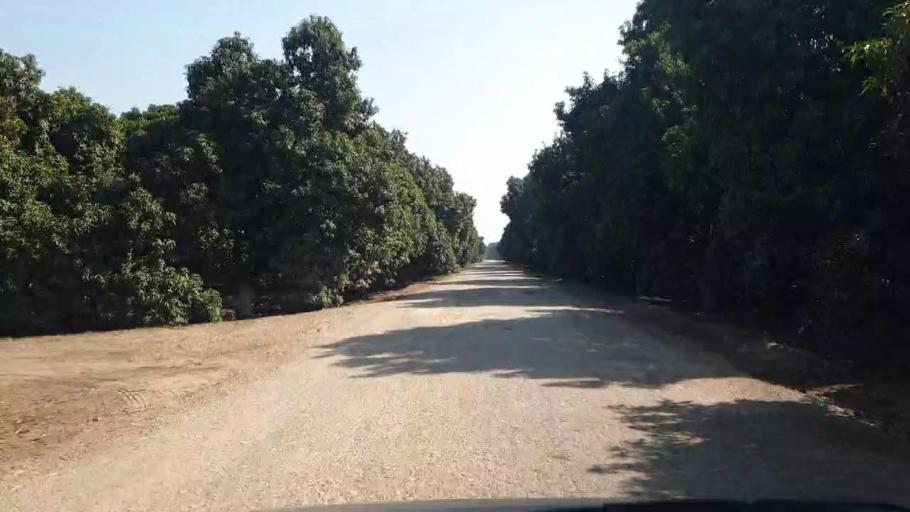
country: PK
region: Sindh
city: Tando Allahyar
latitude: 25.4014
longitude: 68.7761
